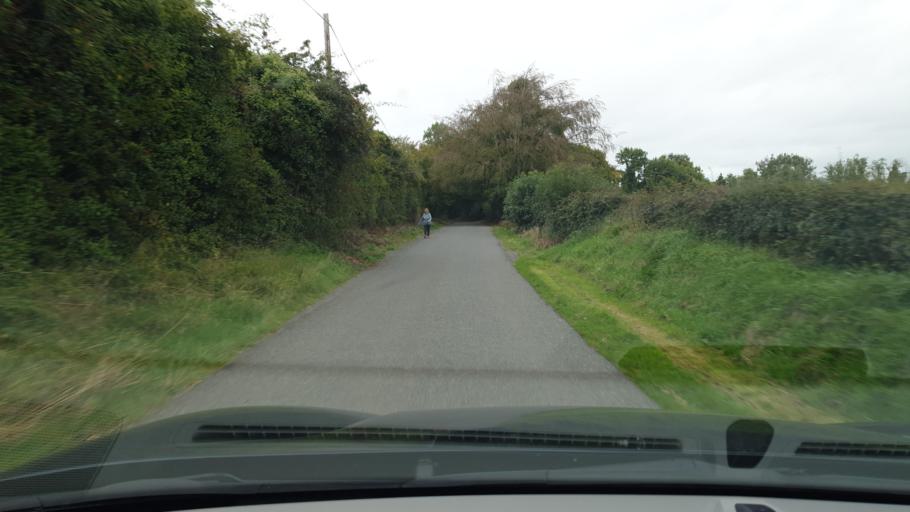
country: IE
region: Leinster
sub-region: An Mhi
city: Dunshaughlin
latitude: 53.5592
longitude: -6.5145
